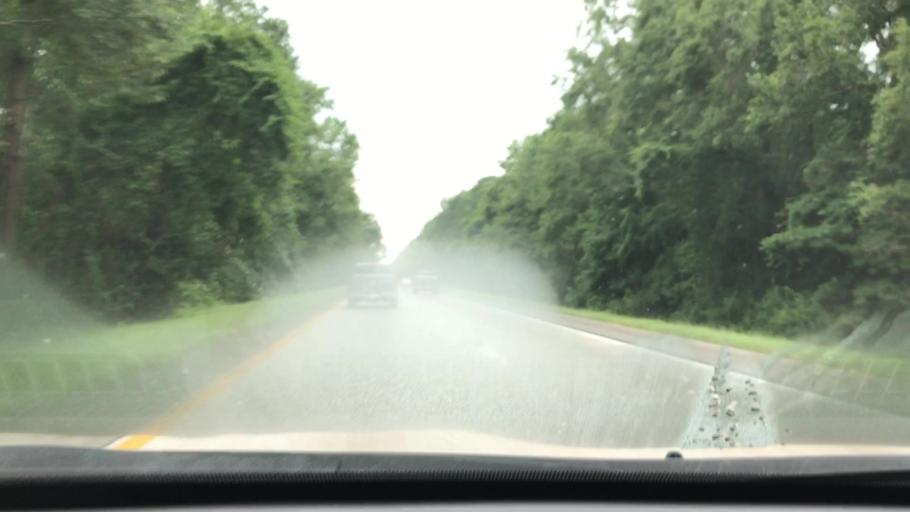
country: US
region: South Carolina
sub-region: Jasper County
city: Ridgeland
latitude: 32.3963
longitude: -81.0213
